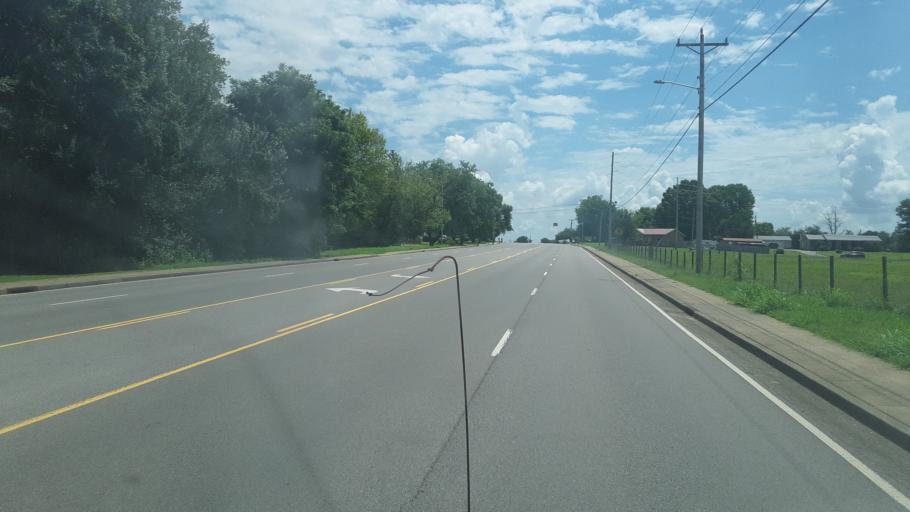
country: US
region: Kentucky
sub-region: Christian County
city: Fort Campbell North
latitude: 36.5756
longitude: -87.4389
